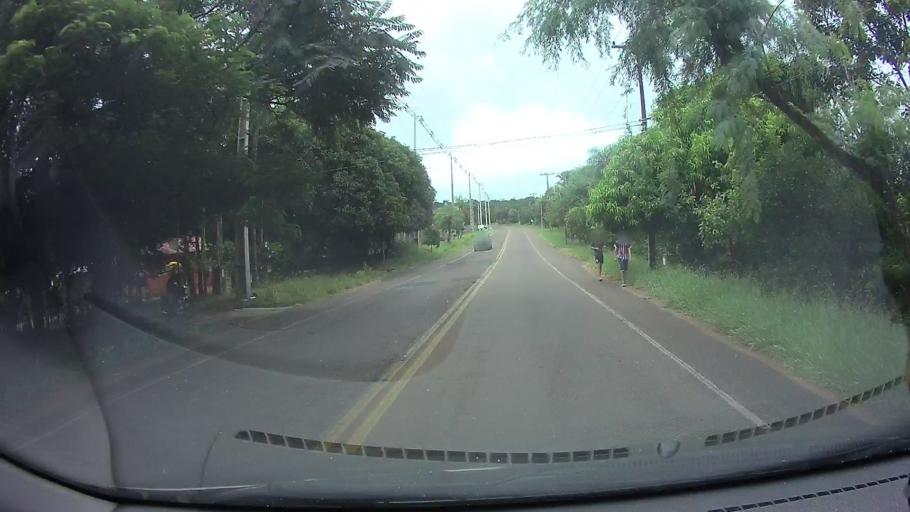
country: PY
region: Cordillera
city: Altos
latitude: -25.2881
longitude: -57.2656
